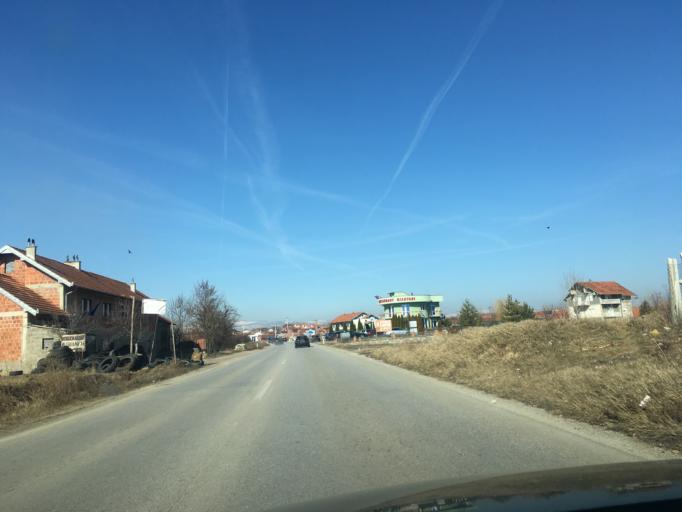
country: XK
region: Prizren
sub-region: Komuna e Malisheves
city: Llazice
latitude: 42.5815
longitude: 20.6946
